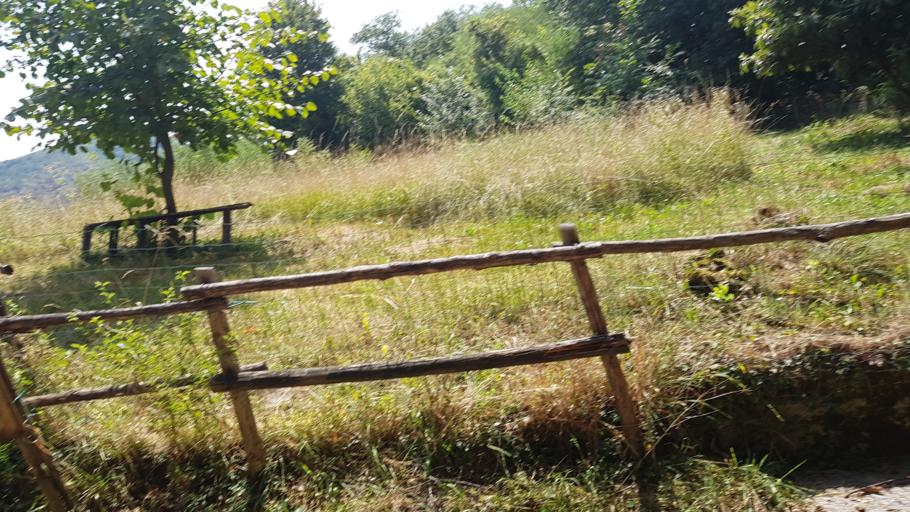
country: IT
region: Friuli Venezia Giulia
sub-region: Provincia di Udine
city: Corno di Rosazzo
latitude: 45.9786
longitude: 13.4631
